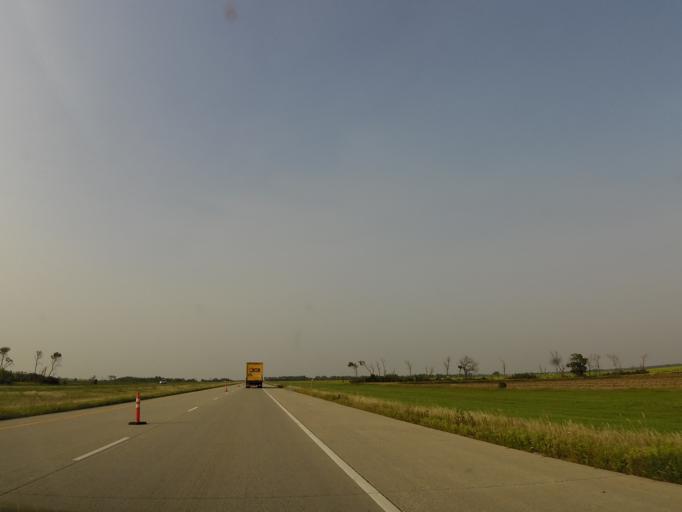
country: US
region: North Dakota
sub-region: Cass County
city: Horace
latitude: 46.6932
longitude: -96.8308
